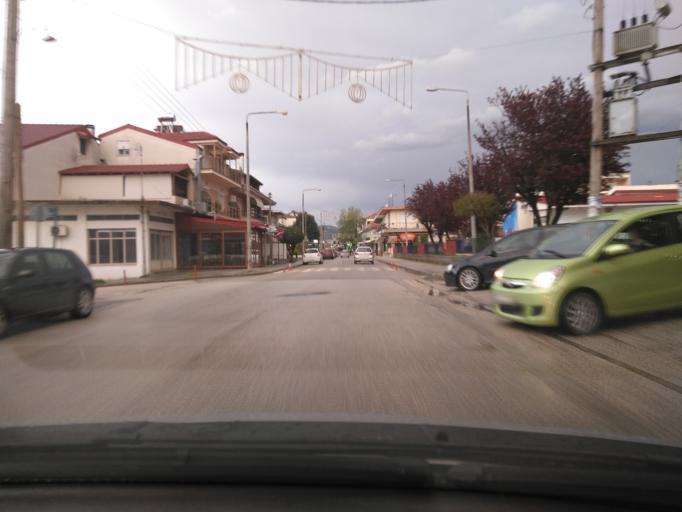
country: GR
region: Epirus
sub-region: Nomos Ioanninon
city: Katsikas
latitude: 39.6243
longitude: 20.8865
